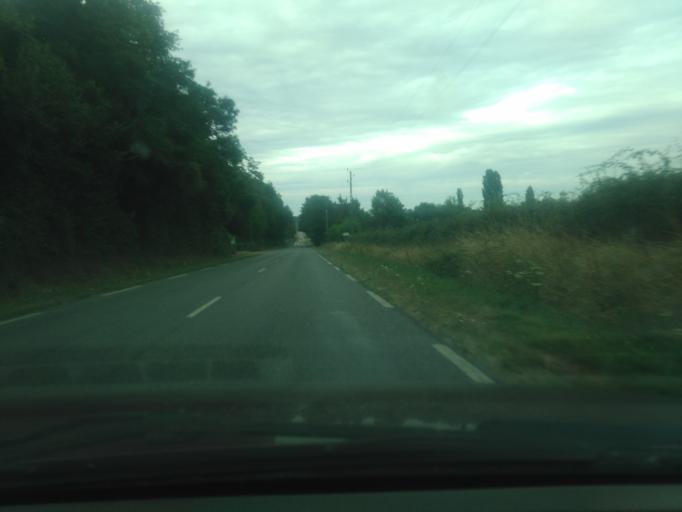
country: FR
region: Bourgogne
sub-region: Departement de la Nievre
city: Decize
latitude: 46.8136
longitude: 3.4492
